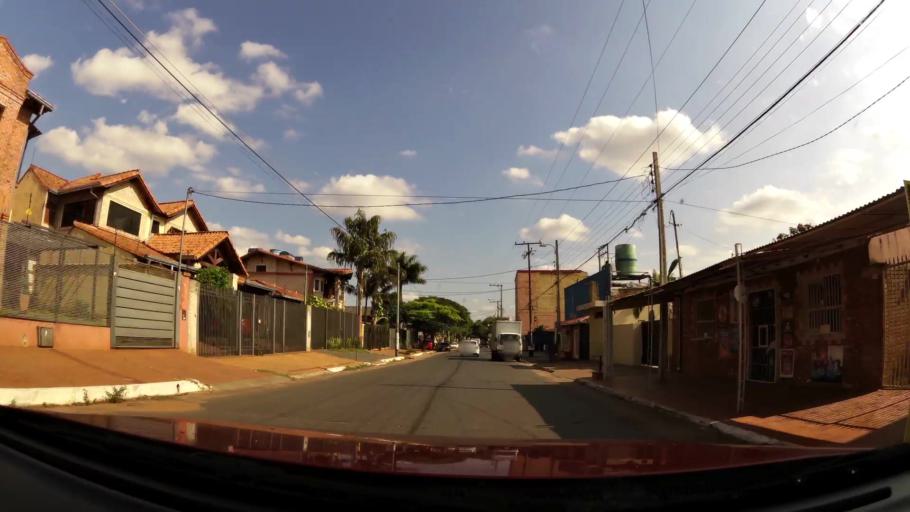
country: PY
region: Central
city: Fernando de la Mora
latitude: -25.3270
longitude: -57.5302
